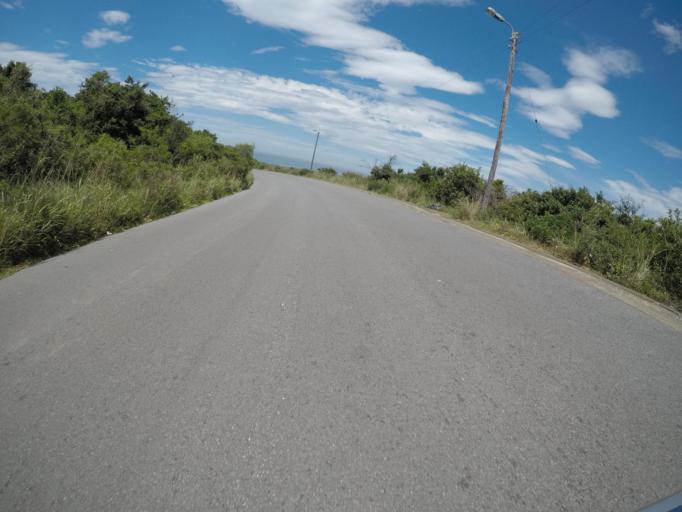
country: ZA
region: Eastern Cape
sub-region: Buffalo City Metropolitan Municipality
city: East London
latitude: -33.0385
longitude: 27.8680
